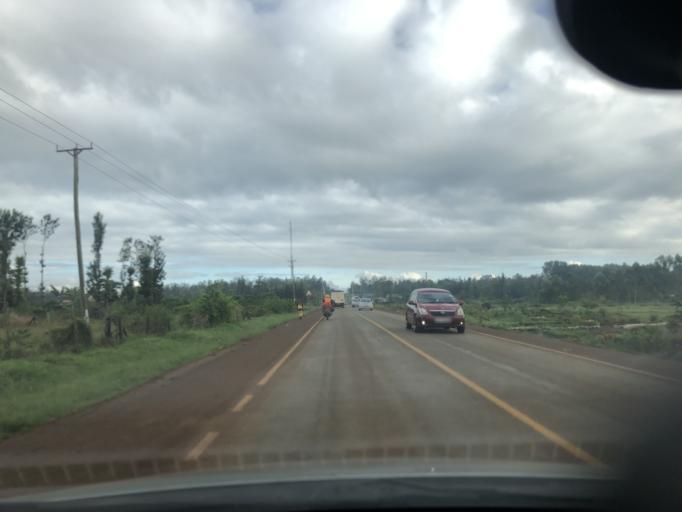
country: KE
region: Murang'a District
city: Maragua
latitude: -0.8405
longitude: 37.1382
